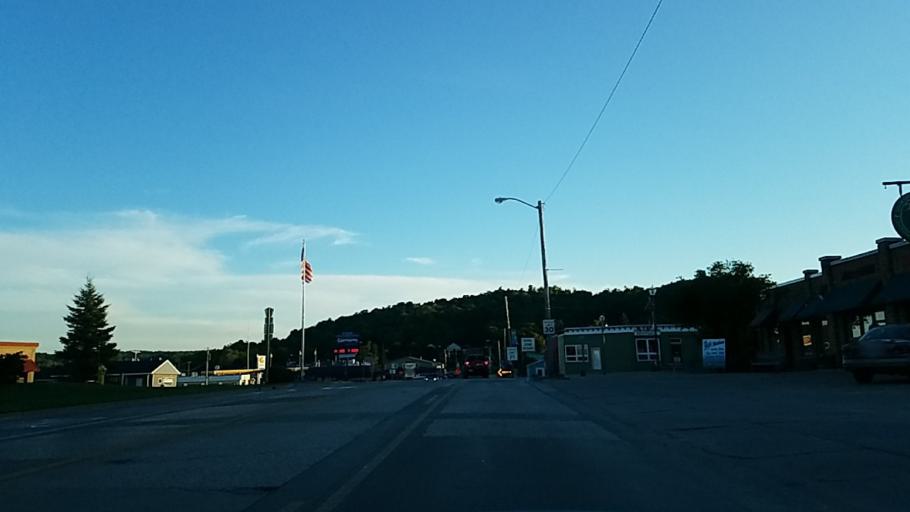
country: US
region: Michigan
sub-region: Alger County
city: Munising
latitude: 46.4094
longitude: -86.6503
